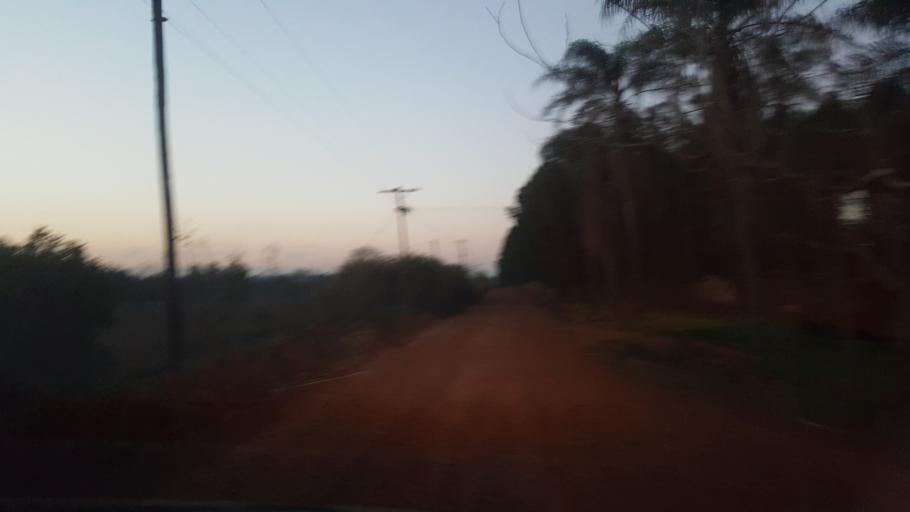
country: AR
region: Misiones
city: Capiovi
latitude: -26.9043
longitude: -55.0503
